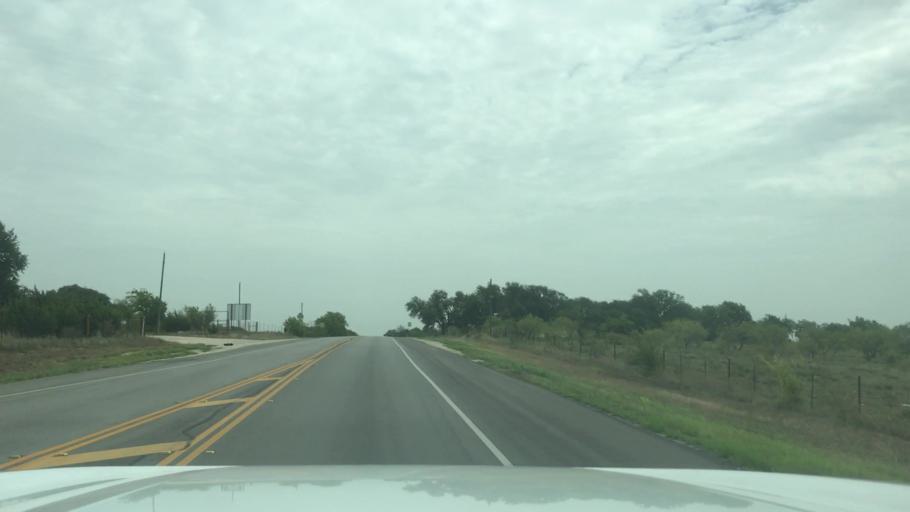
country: US
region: Texas
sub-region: Erath County
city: Dublin
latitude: 32.0856
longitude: -98.3174
